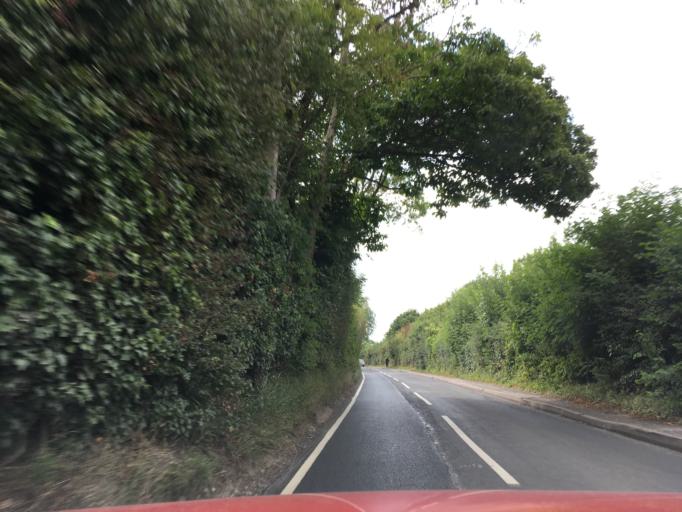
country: GB
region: England
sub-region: Kent
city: Maidstone
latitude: 51.2535
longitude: 0.4744
